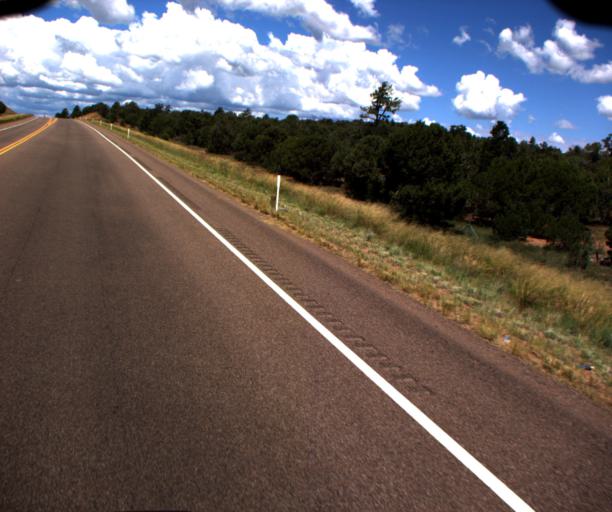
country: US
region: Arizona
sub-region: Navajo County
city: Heber-Overgaard
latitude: 34.3665
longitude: -110.3620
